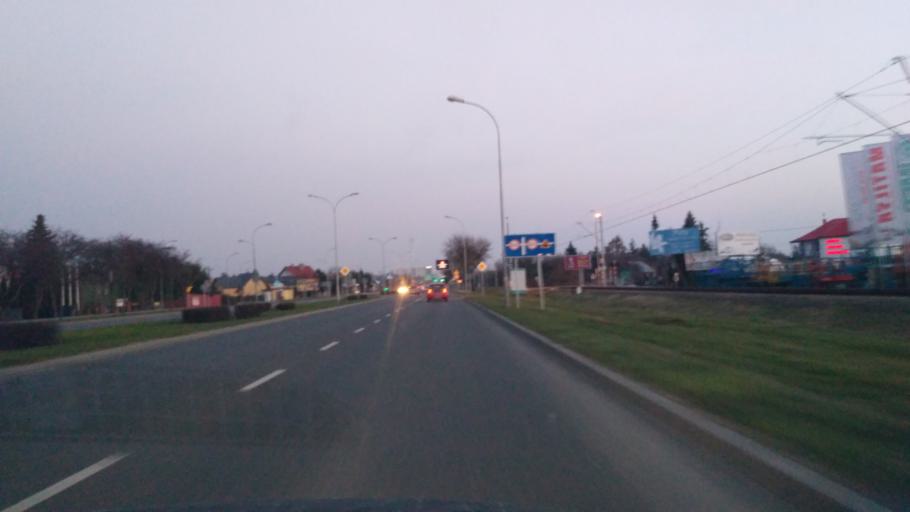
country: PL
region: Subcarpathian Voivodeship
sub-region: Rzeszow
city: Rzeszow
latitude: 50.0705
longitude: 21.9895
